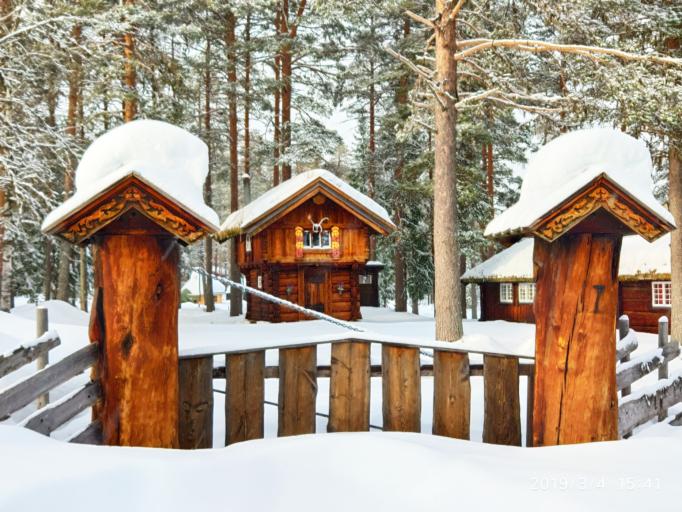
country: NO
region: Hedmark
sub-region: Trysil
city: Innbygda
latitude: 61.2574
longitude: 12.5305
